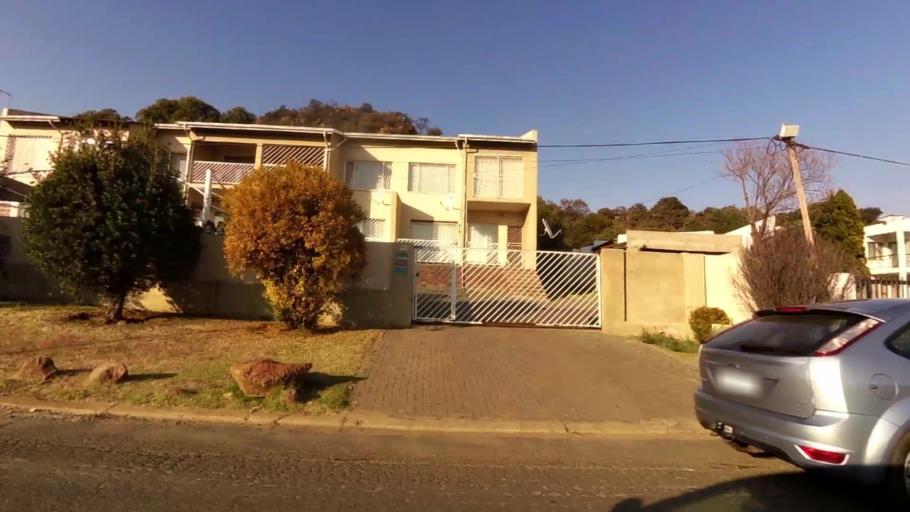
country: ZA
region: Gauteng
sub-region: City of Johannesburg Metropolitan Municipality
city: Soweto
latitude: -26.2765
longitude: 27.9587
